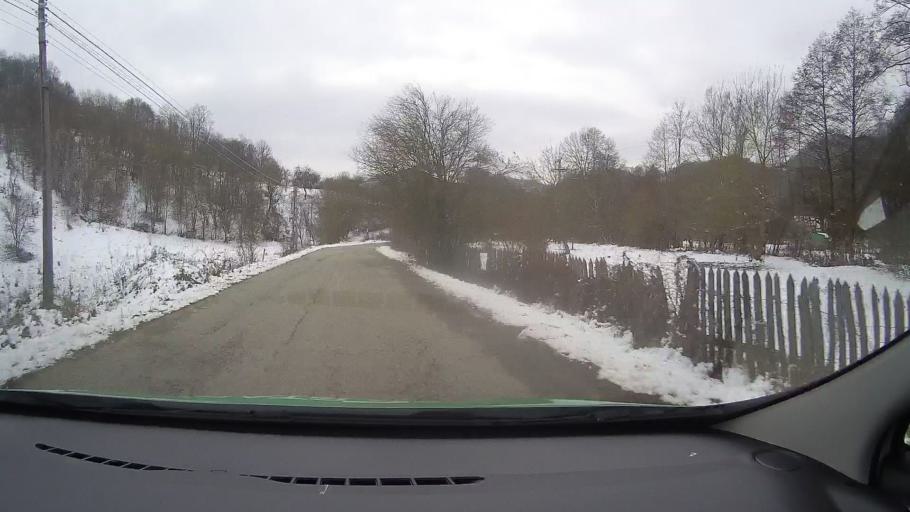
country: RO
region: Hunedoara
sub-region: Comuna Balsa
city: Balsa
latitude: 46.0494
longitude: 23.0707
